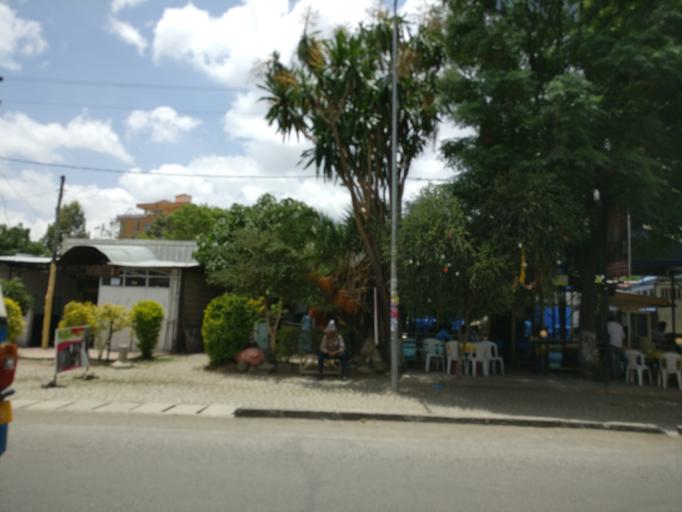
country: ET
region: Oromiya
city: Bishoftu
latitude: 8.7514
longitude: 38.9597
